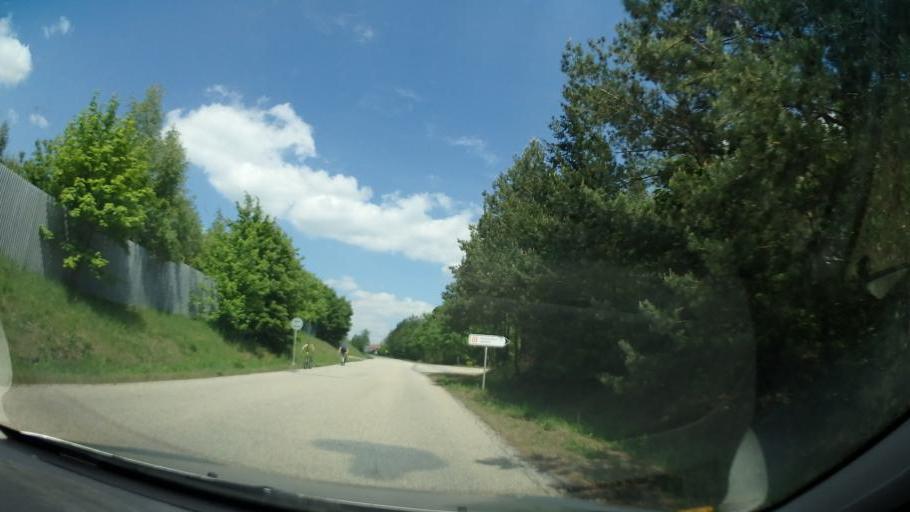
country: CZ
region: Vysocina
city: Mohelno
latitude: 49.1295
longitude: 16.1292
